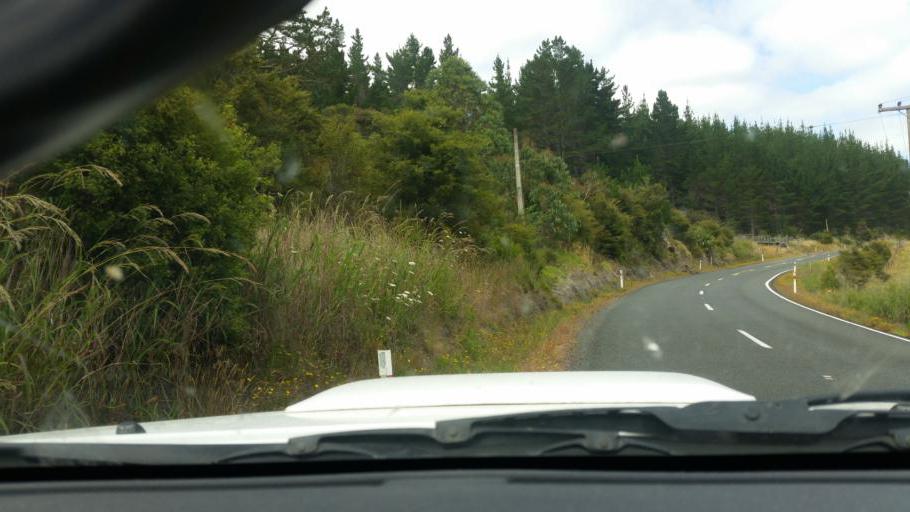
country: NZ
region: Northland
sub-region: Kaipara District
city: Dargaville
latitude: -35.8159
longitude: 173.7261
